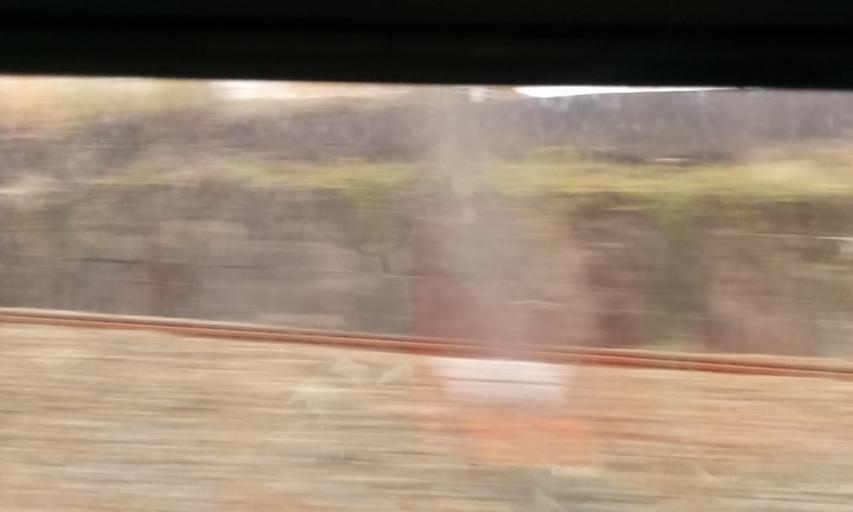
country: JP
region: Gifu
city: Nakatsugawa
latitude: 35.5041
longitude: 137.5044
